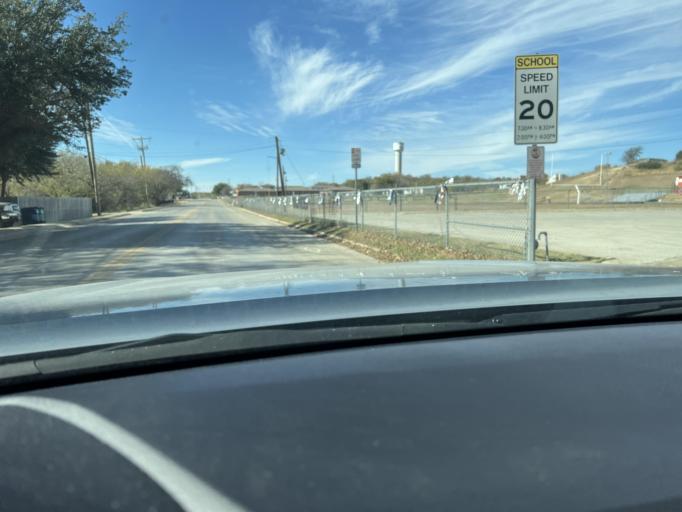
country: US
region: Texas
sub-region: Eastland County
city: Eastland
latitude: 32.3955
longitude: -98.8268
